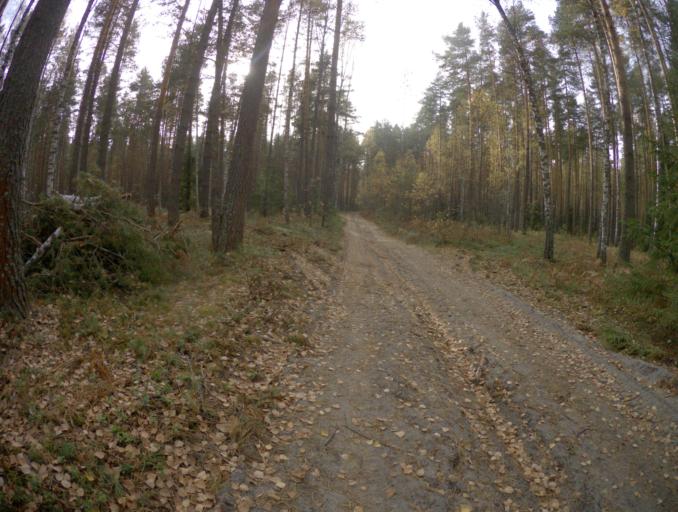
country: RU
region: Vladimir
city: Sobinka
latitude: 55.9194
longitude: 40.1353
